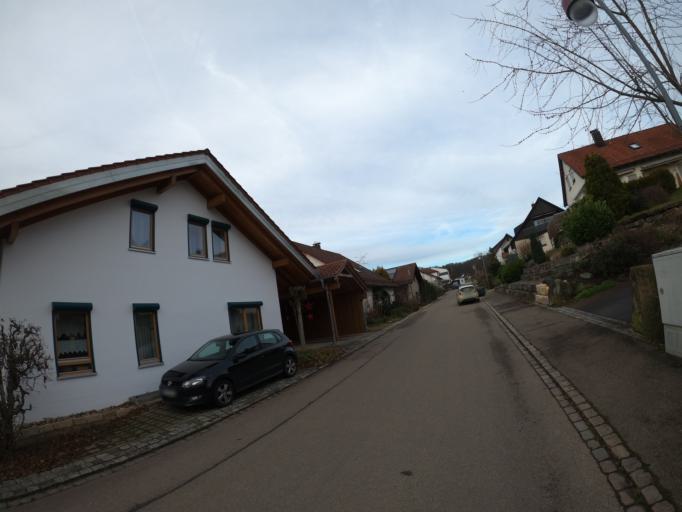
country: DE
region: Baden-Wuerttemberg
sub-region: Regierungsbezirk Stuttgart
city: Ottenbach
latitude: 48.7343
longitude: 9.7441
